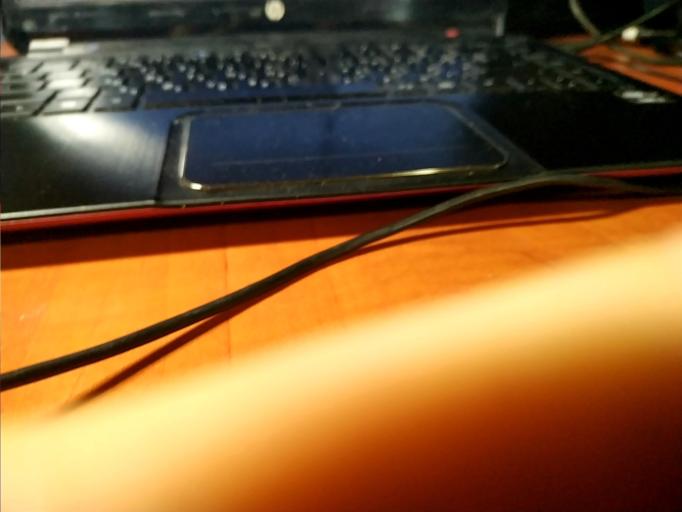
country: RU
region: Tverskaya
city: Rameshki
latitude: 57.1485
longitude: 36.0847
